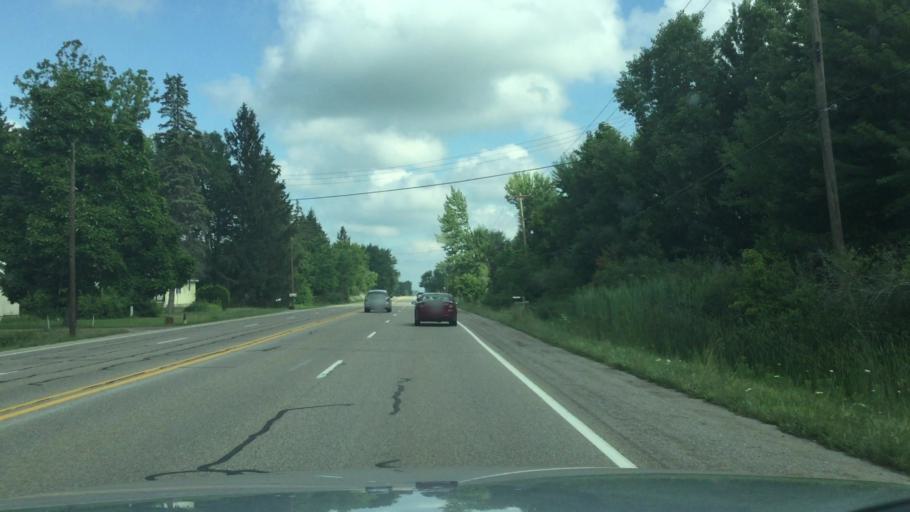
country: US
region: Michigan
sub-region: Genesee County
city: Clio
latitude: 43.2169
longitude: -83.7442
